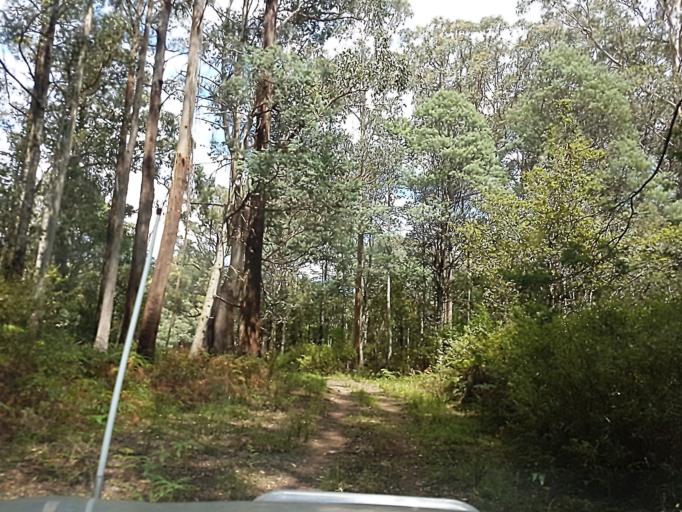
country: AU
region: Victoria
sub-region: East Gippsland
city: Lakes Entrance
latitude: -37.3319
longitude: 148.3197
